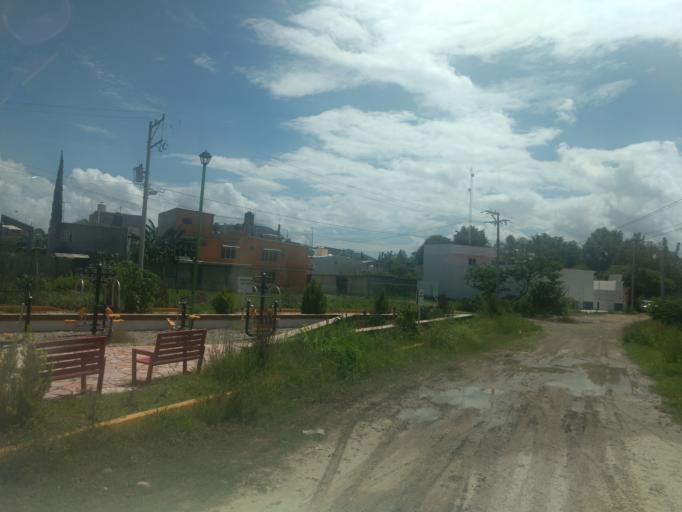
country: MX
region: Oaxaca
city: Ciudad de Huajuapam de Leon
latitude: 17.8009
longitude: -97.7757
